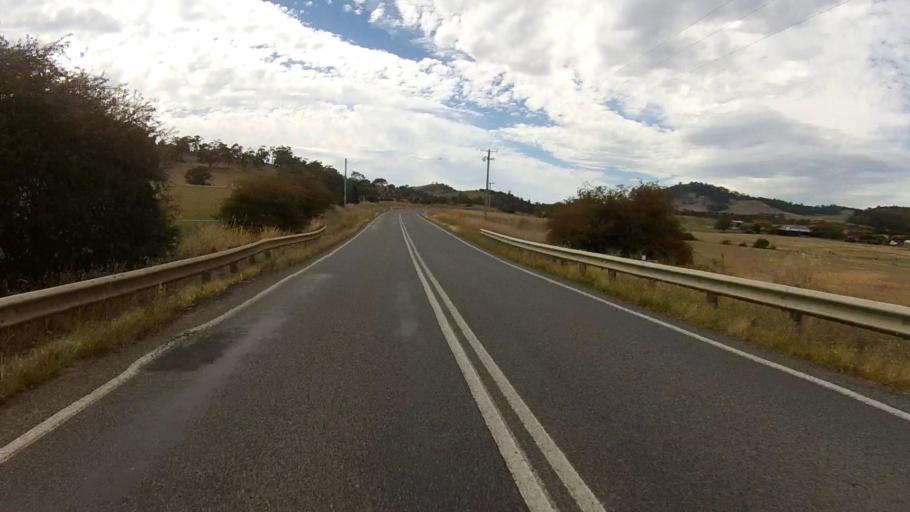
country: AU
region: Tasmania
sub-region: Sorell
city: Sorell
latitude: -42.6924
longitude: 147.4742
